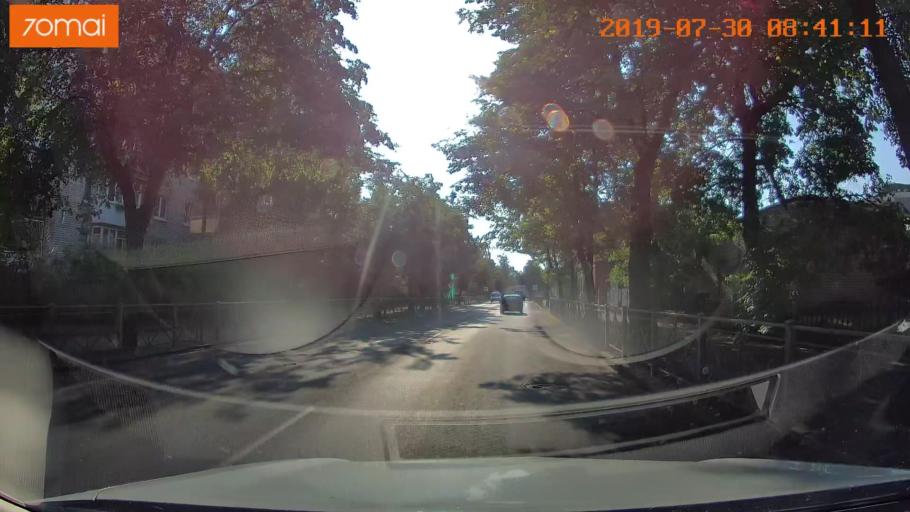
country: RU
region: Kaliningrad
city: Chernyakhovsk
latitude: 54.6307
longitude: 21.8154
